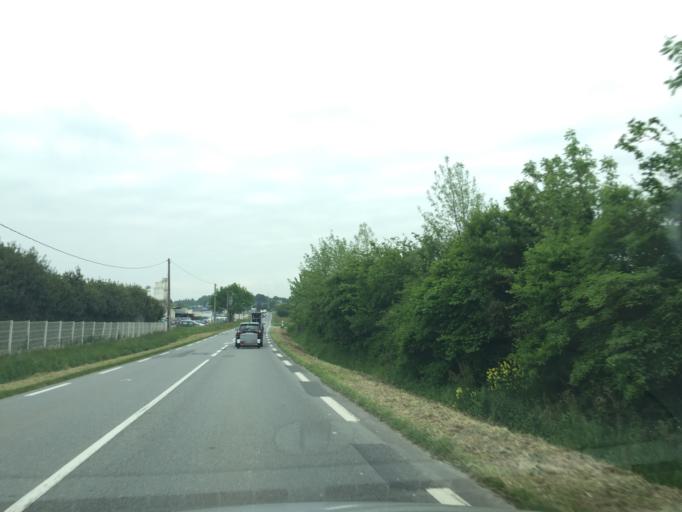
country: FR
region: Brittany
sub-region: Departement des Cotes-d'Armor
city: Lamballe
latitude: 48.4831
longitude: -2.4919
